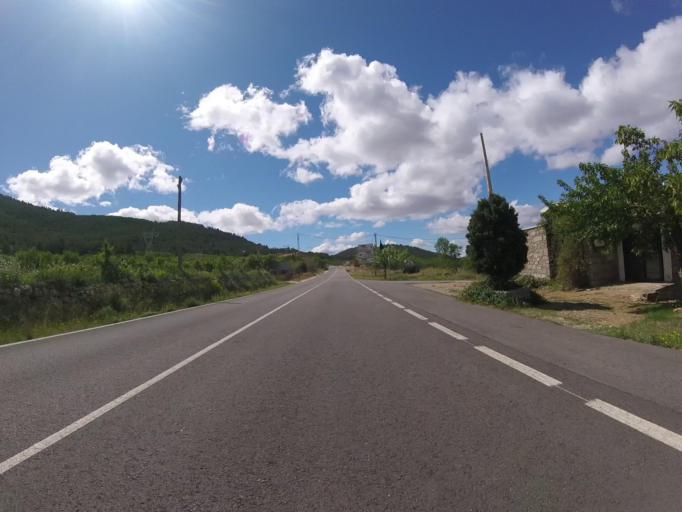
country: ES
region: Valencia
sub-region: Provincia de Castello
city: Culla
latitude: 40.2839
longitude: -0.1124
